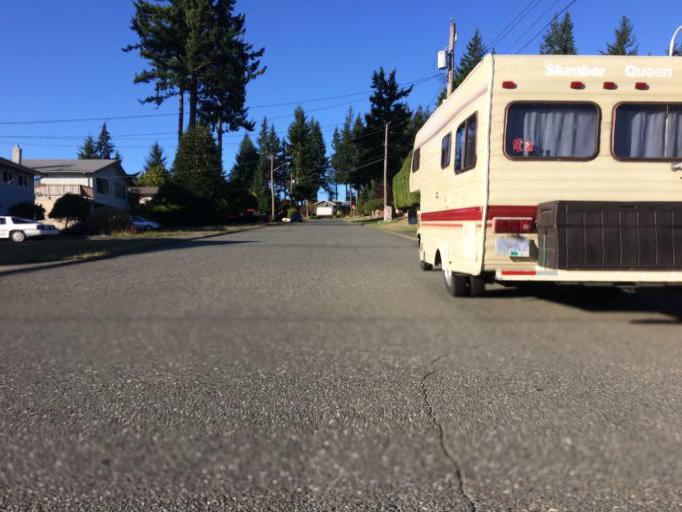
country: CA
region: British Columbia
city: Campbell River
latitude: 49.9846
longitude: -125.2341
